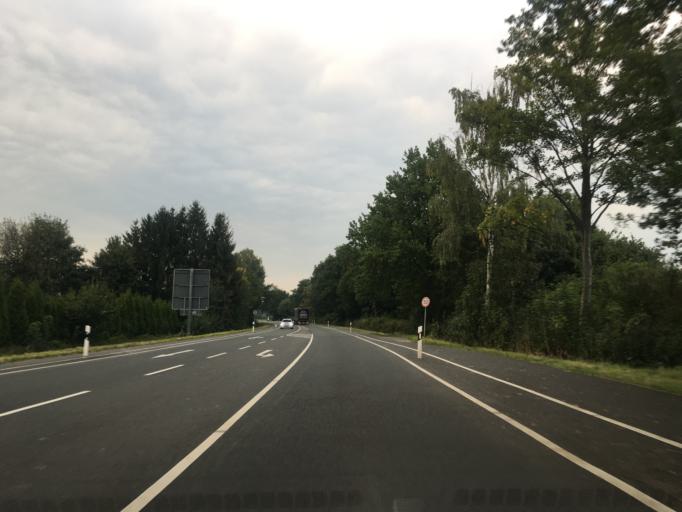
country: DE
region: North Rhine-Westphalia
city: Selm
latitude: 51.7059
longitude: 7.4585
